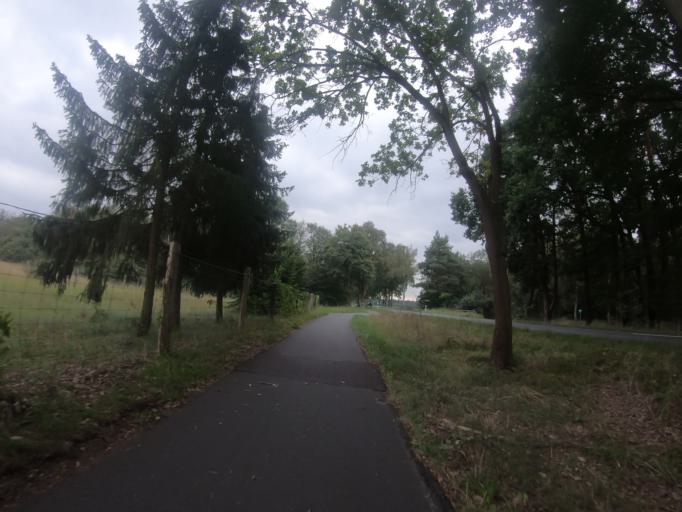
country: DE
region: Lower Saxony
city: Ribbesbuttel
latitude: 52.4455
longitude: 10.5016
